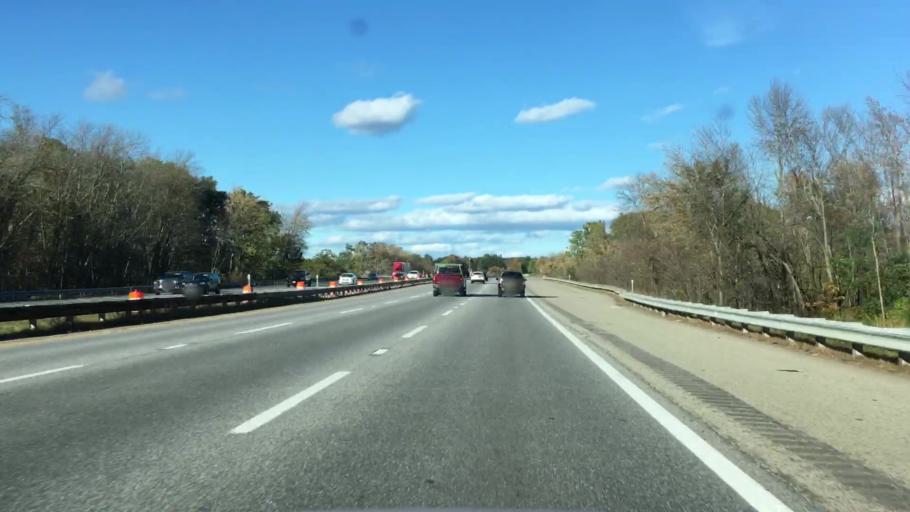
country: US
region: Maine
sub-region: York County
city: Biddeford
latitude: 43.4966
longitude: -70.4895
